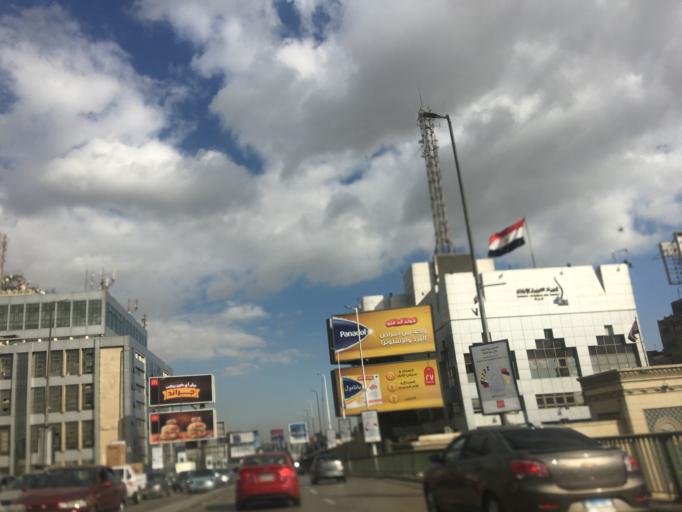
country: EG
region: Muhafazat al Qahirah
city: Cairo
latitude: 30.0626
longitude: 31.2478
